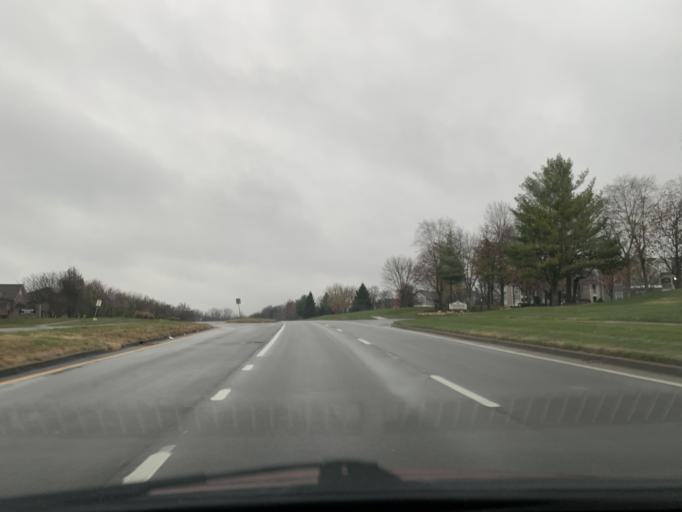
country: US
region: Kentucky
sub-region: Jefferson County
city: Hurstbourne Acres
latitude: 38.2002
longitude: -85.6028
